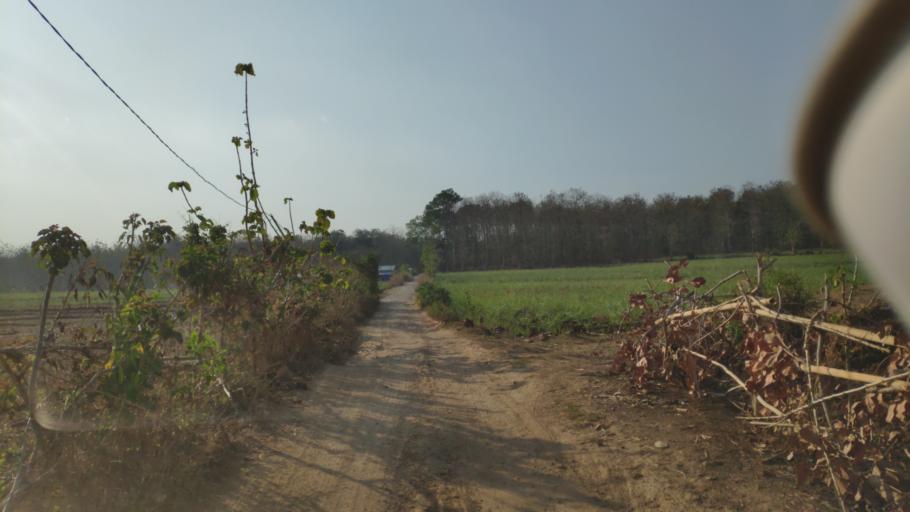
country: ID
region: Central Java
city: Pelem
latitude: -6.9954
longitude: 111.1890
